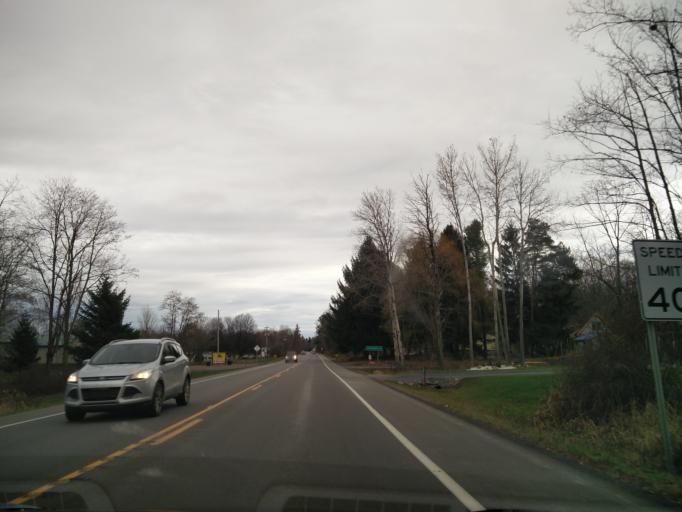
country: US
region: New York
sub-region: Tompkins County
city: Trumansburg
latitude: 42.5140
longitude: -76.6214
